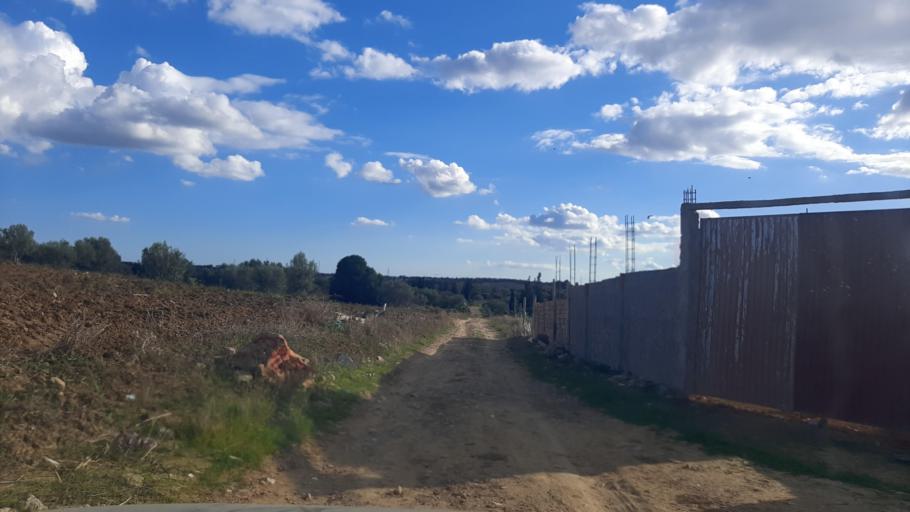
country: TN
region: Nabul
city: Bu `Urqub
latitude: 36.4539
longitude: 10.4994
